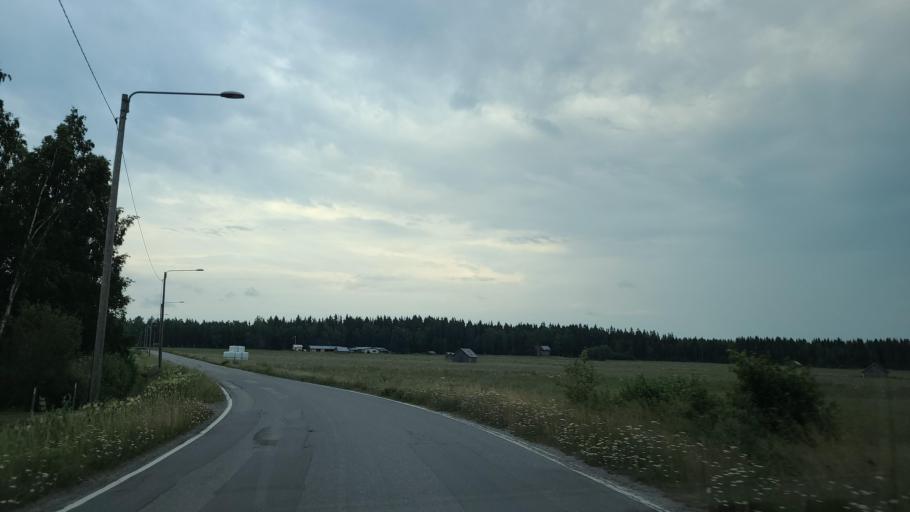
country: FI
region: Ostrobothnia
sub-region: Vaasa
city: Replot
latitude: 63.1844
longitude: 21.2945
